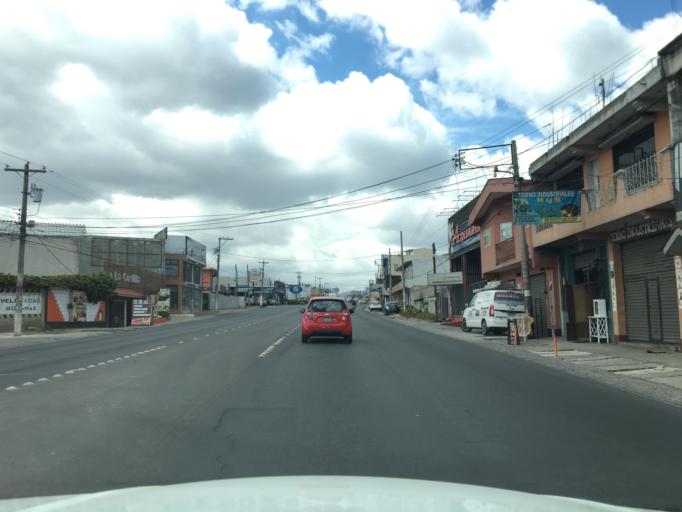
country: GT
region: Quetzaltenango
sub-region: Municipio de La Esperanza
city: La Esperanza
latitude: 14.8633
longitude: -91.5553
